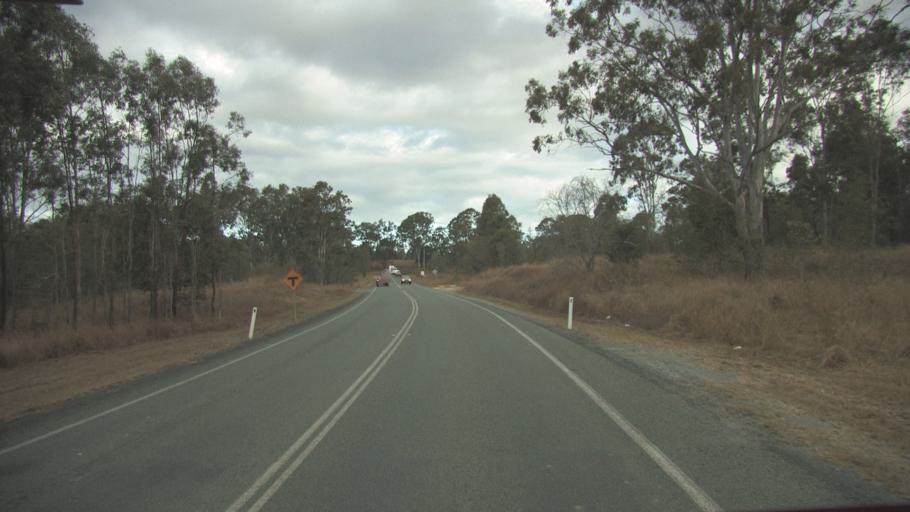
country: AU
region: Queensland
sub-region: Logan
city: Cedar Vale
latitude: -27.9093
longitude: 153.0900
